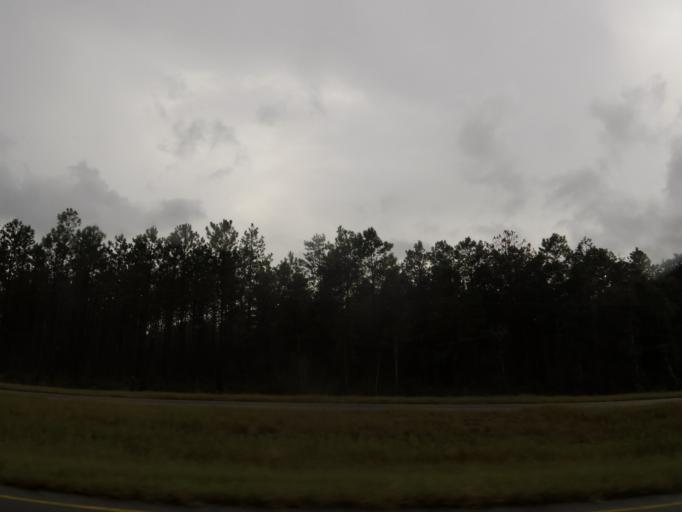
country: US
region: Georgia
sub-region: Wayne County
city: Jesup
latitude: 31.4612
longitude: -81.7099
